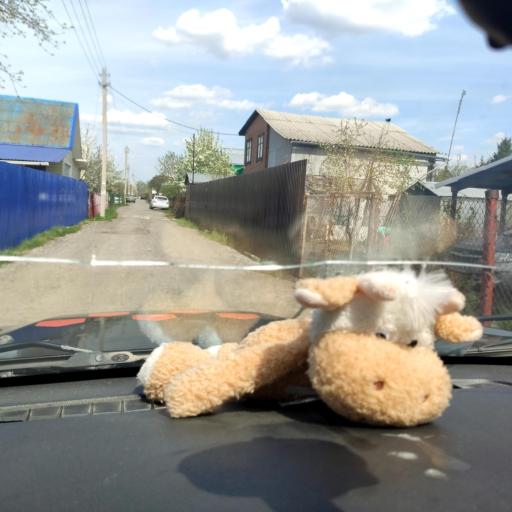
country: RU
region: Samara
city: Podstepki
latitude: 53.6022
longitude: 49.2168
